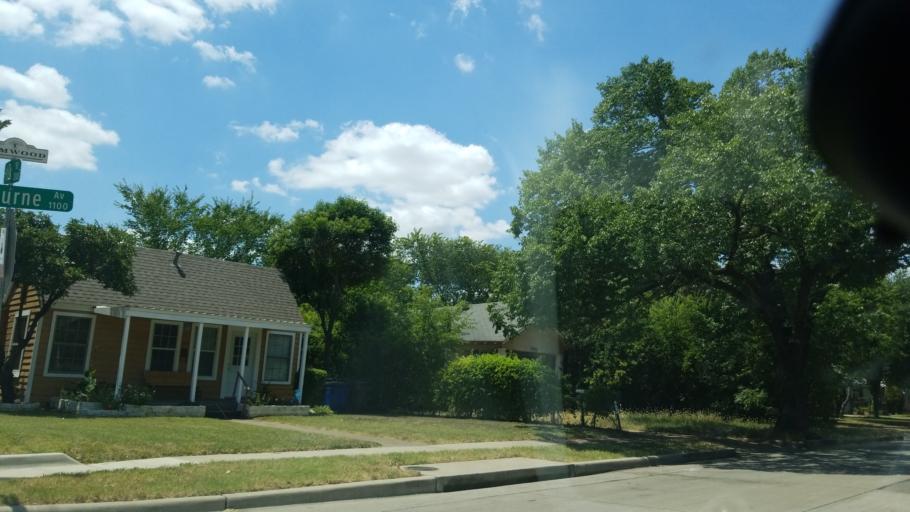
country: US
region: Texas
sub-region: Dallas County
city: Cockrell Hill
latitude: 32.7233
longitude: -96.8401
